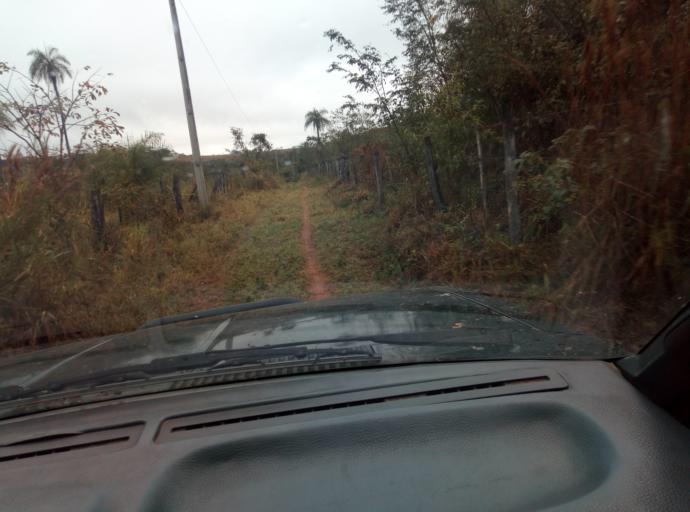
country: PY
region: Caaguazu
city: Carayao
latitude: -25.1949
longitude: -56.3544
